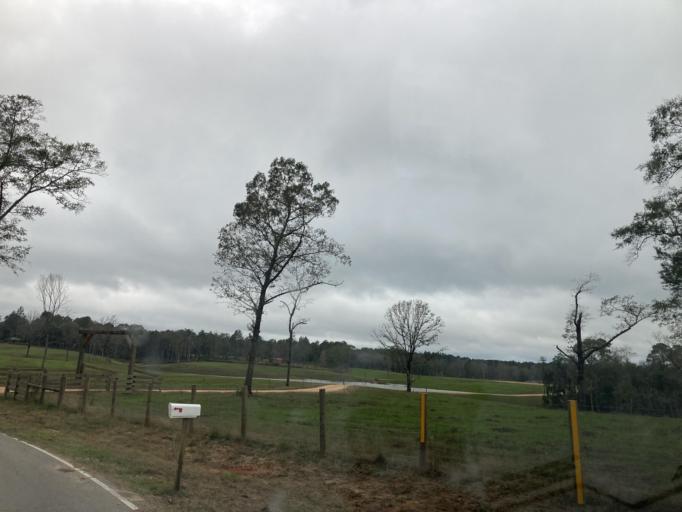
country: US
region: Mississippi
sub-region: Lamar County
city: Purvis
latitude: 31.1823
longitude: -89.4590
